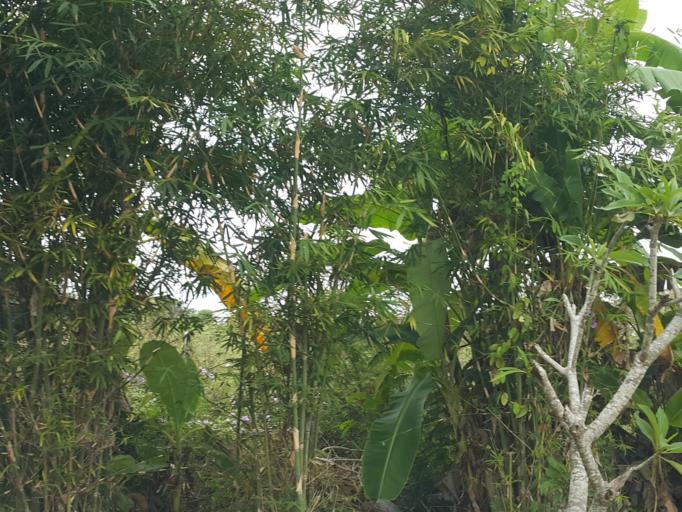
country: TH
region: Lampang
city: Lampang
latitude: 18.3081
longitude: 99.4994
